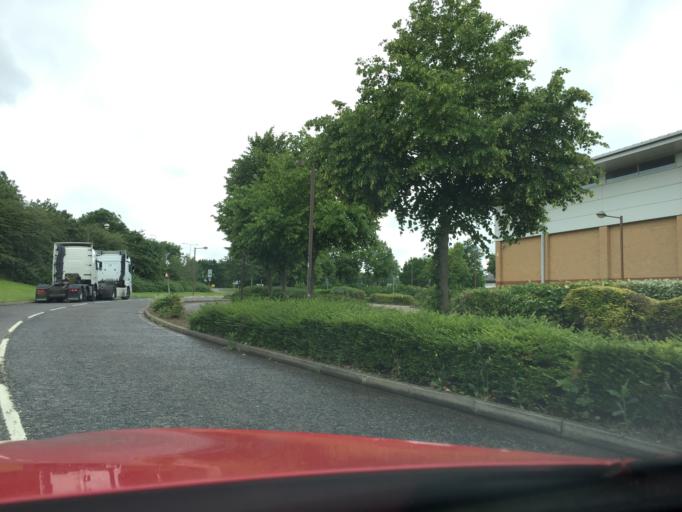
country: GB
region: England
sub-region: Milton Keynes
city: Wavendon
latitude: 52.0347
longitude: -0.6862
